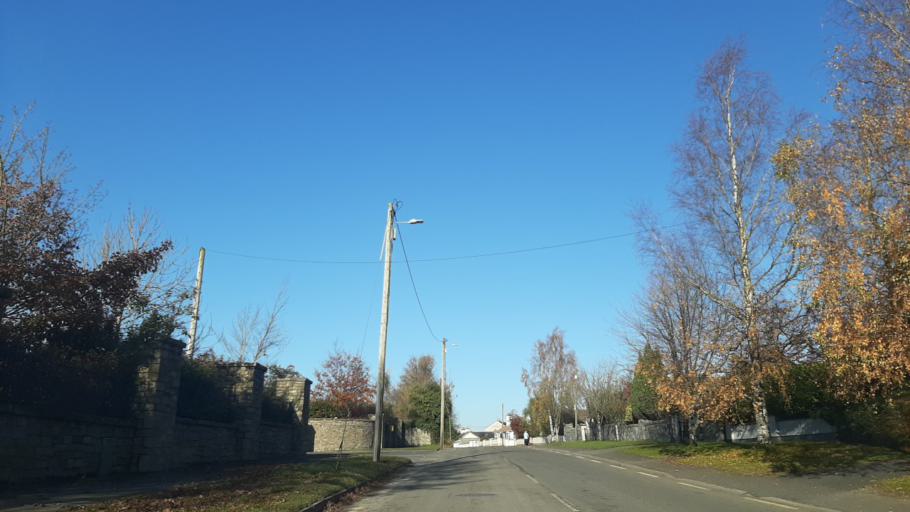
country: IE
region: Leinster
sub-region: Kildare
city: Rathangan
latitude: 53.2196
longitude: -7.0038
